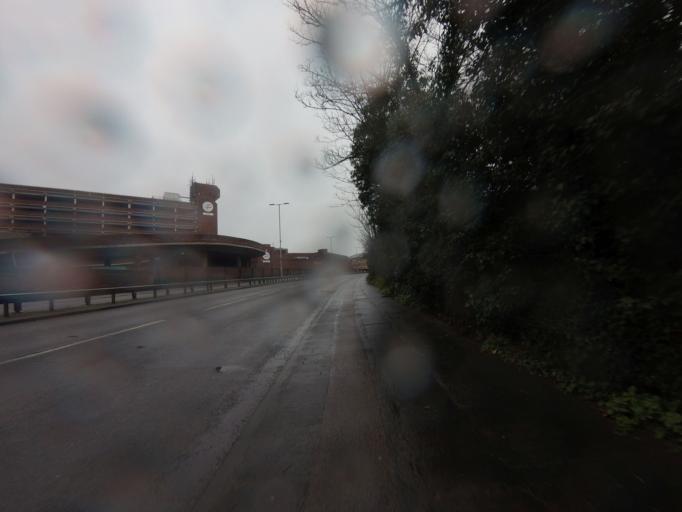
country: GB
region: England
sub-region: Hertfordshire
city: Waltham Cross
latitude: 51.6864
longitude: -0.0306
